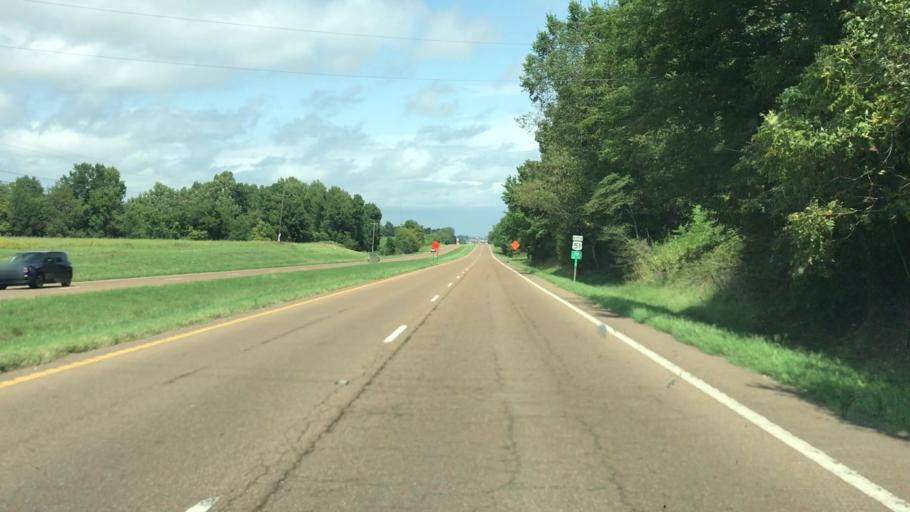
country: US
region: Tennessee
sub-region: Obion County
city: Englewood
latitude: 36.3782
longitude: -89.1145
